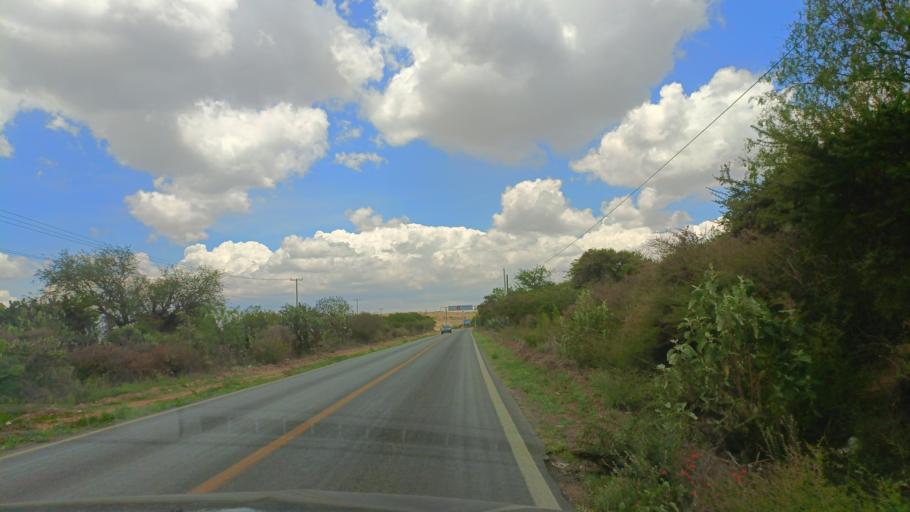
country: MX
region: Guanajuato
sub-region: San Luis de la Paz
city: San Ignacio
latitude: 21.2367
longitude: -100.4908
